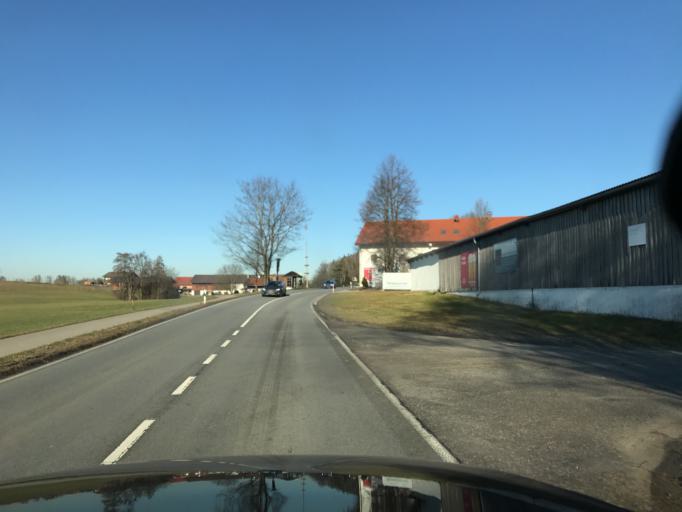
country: DE
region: Bavaria
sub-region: Upper Bavaria
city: Rosenheim
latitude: 47.8755
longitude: 12.1528
